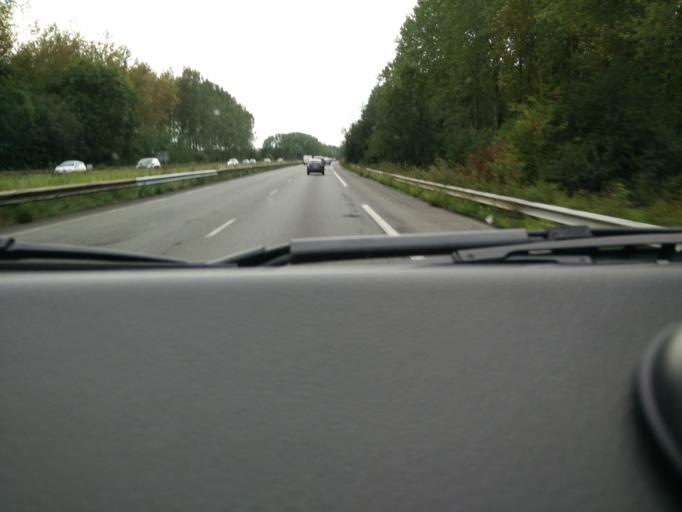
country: FR
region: Nord-Pas-de-Calais
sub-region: Departement du Nord
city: Rosult
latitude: 50.4375
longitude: 3.3628
